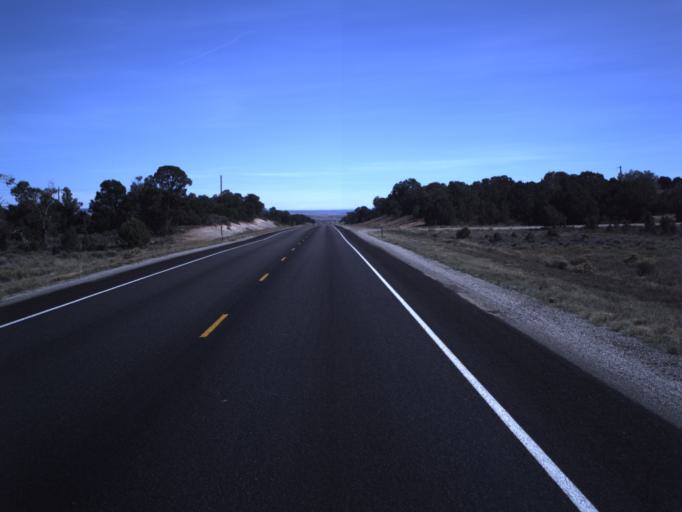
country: US
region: Colorado
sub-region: Dolores County
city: Dove Creek
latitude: 37.8271
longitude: -109.0789
